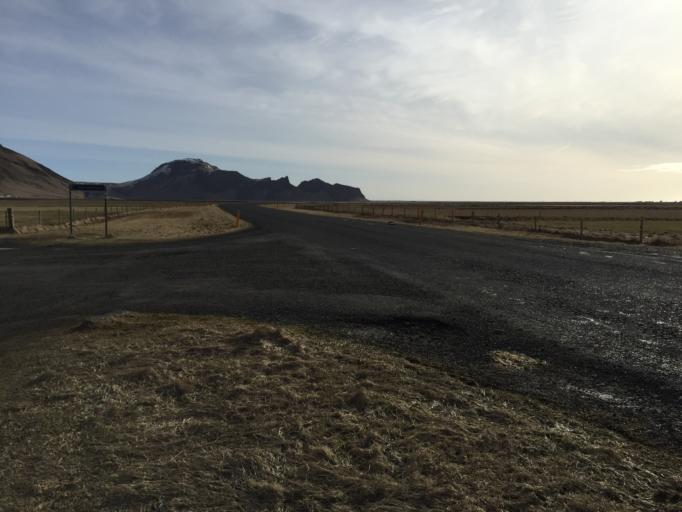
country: IS
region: South
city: Vestmannaeyjar
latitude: 63.5428
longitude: -19.6629
